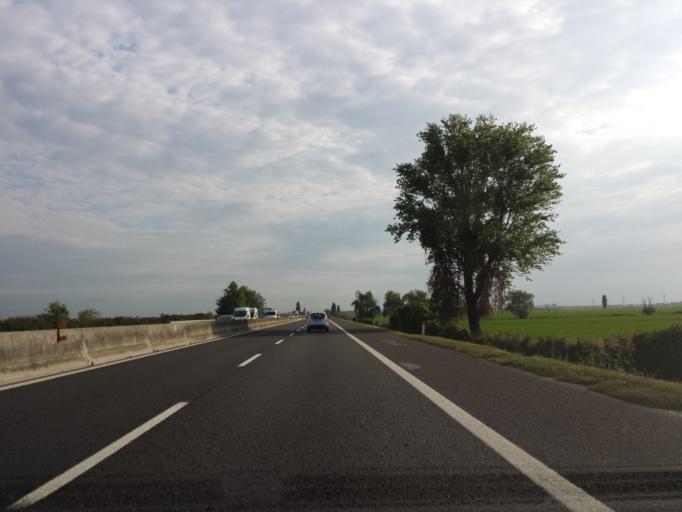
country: IT
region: Veneto
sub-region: Provincia di Padova
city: Pozzonovo
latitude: 45.1790
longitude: 11.7762
